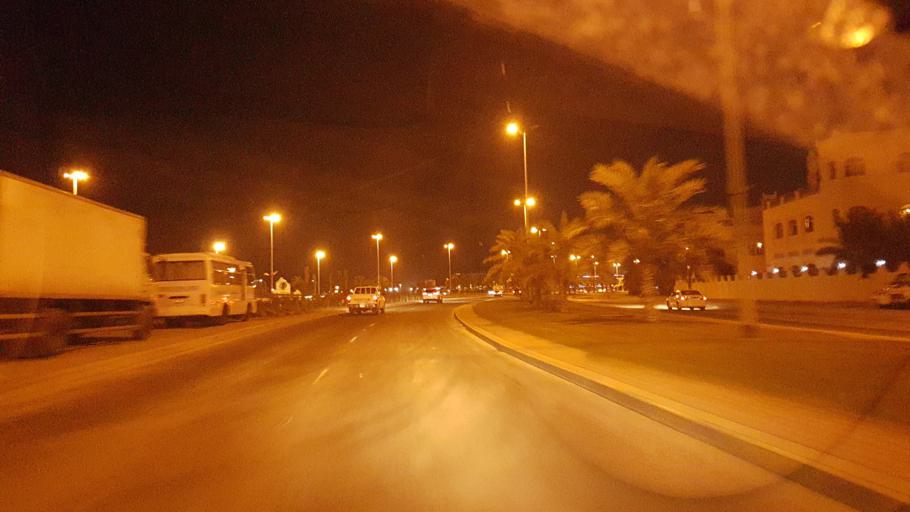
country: BH
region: Muharraq
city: Al Muharraq
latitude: 26.2524
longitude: 50.6051
